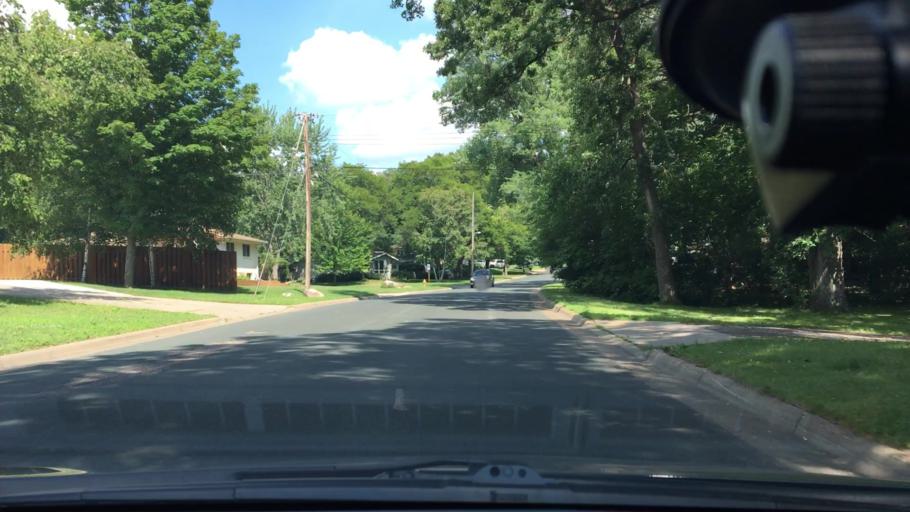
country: US
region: Minnesota
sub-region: Hennepin County
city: Golden Valley
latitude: 44.9974
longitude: -93.3828
